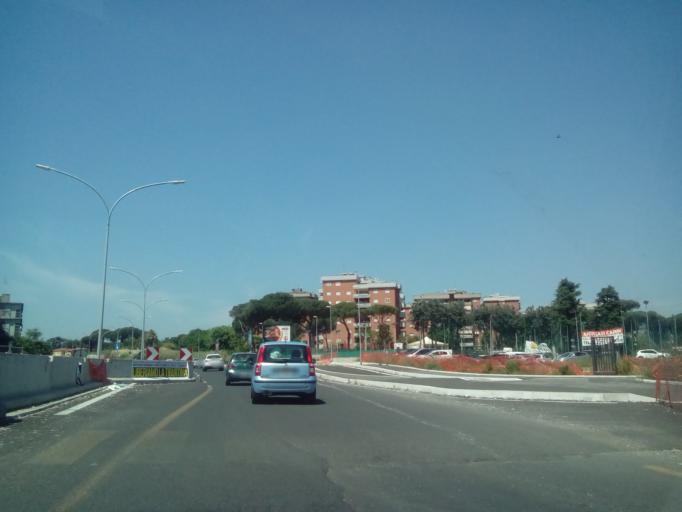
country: IT
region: Latium
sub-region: Citta metropolitana di Roma Capitale
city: Colle Verde
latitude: 41.9326
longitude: 12.5845
